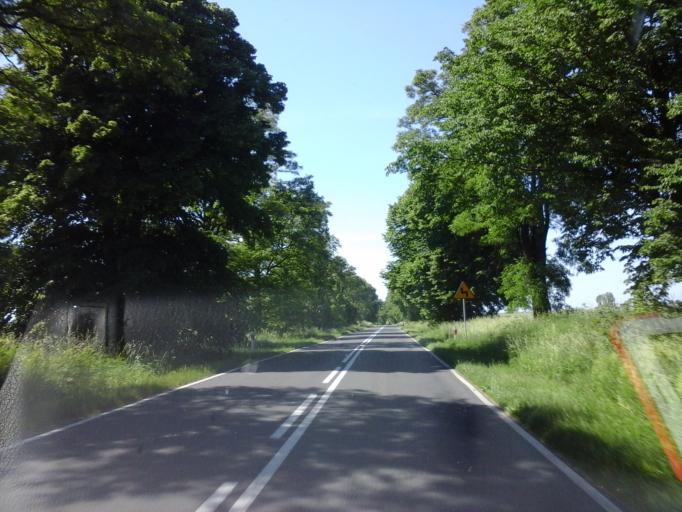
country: PL
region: West Pomeranian Voivodeship
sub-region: Powiat choszczenski
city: Krzecin
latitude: 53.1369
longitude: 15.5218
